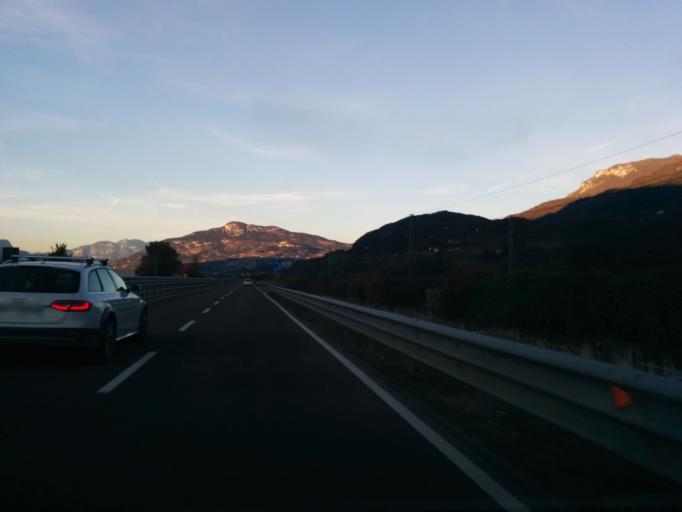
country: IT
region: Trentino-Alto Adige
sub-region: Provincia di Trento
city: Mattarello
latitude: 46.0148
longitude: 11.1268
